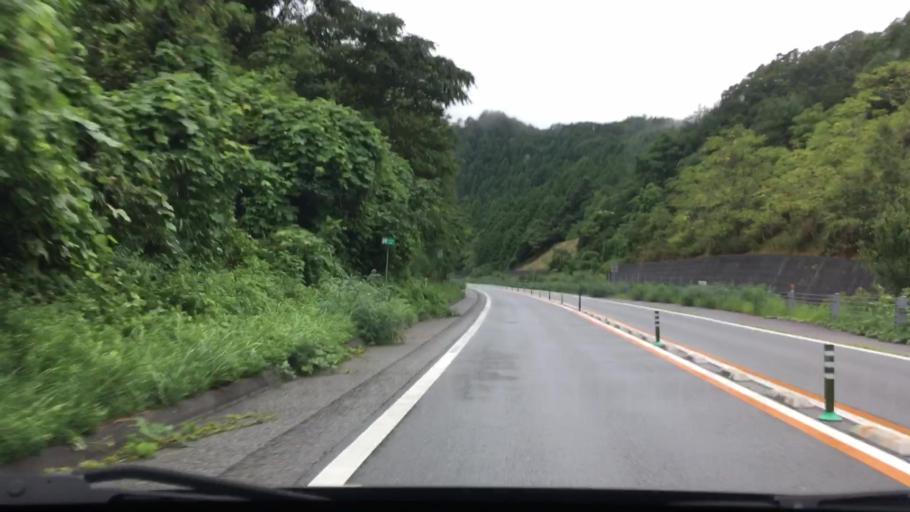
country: JP
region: Hyogo
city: Toyooka
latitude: 35.2593
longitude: 134.7959
